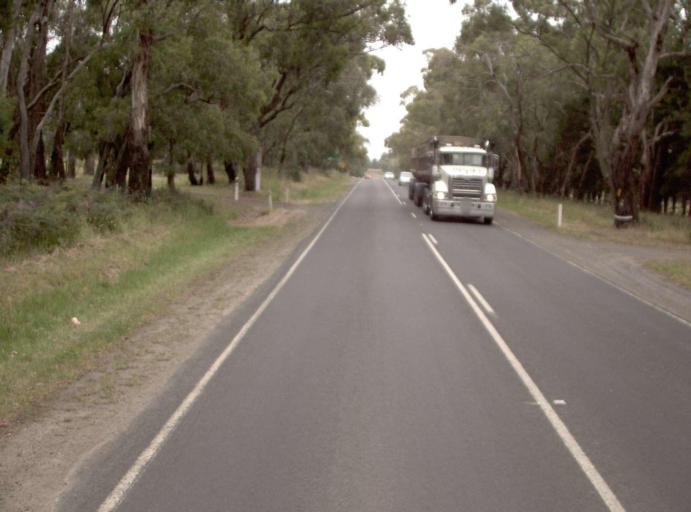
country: AU
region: Victoria
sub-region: Latrobe
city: Traralgon
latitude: -38.2528
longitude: 146.4926
